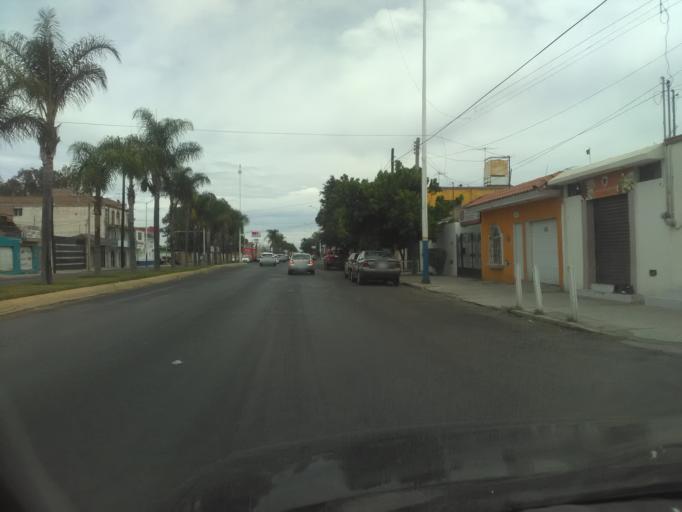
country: MX
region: Durango
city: Victoria de Durango
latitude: 24.0269
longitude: -104.6321
